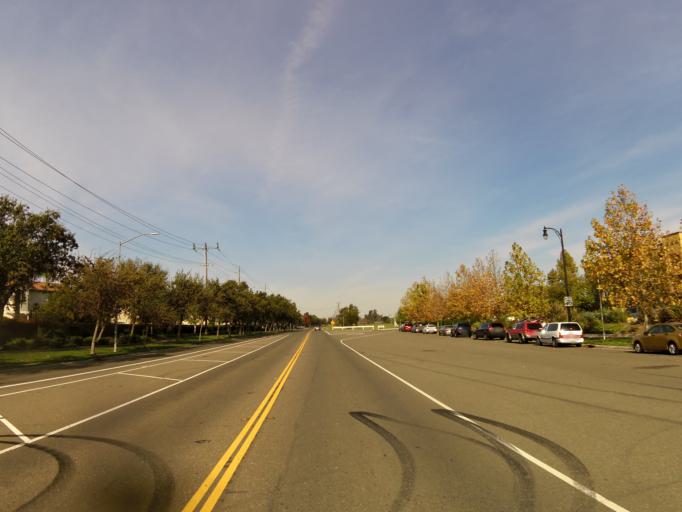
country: US
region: California
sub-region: Sacramento County
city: Laguna
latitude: 38.3800
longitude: -121.4174
